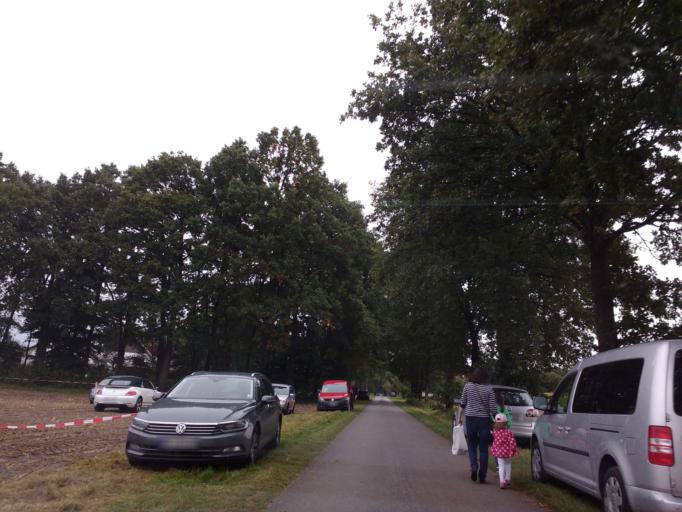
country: DE
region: North Rhine-Westphalia
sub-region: Regierungsbezirk Detmold
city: Delbruck
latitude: 51.7551
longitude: 8.6155
